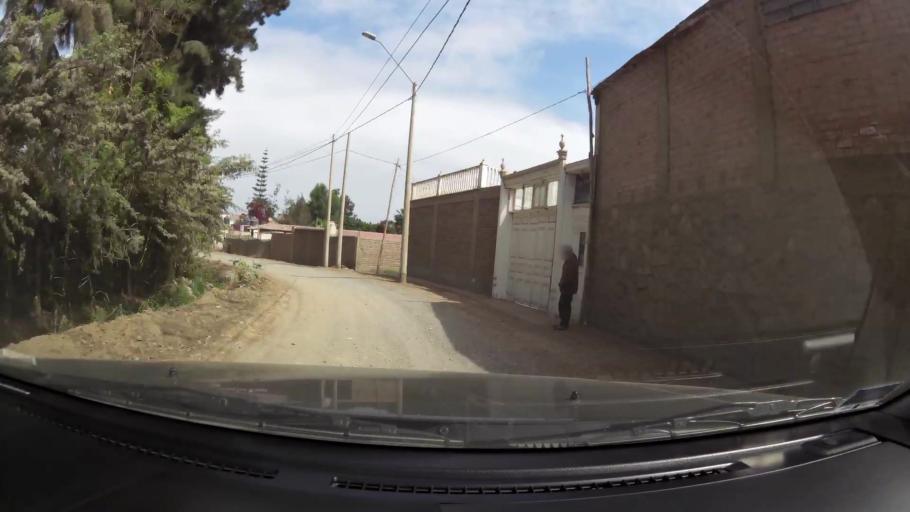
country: PE
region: Lima
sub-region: Provincia de Canete
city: Asia
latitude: -12.7337
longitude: -76.6238
